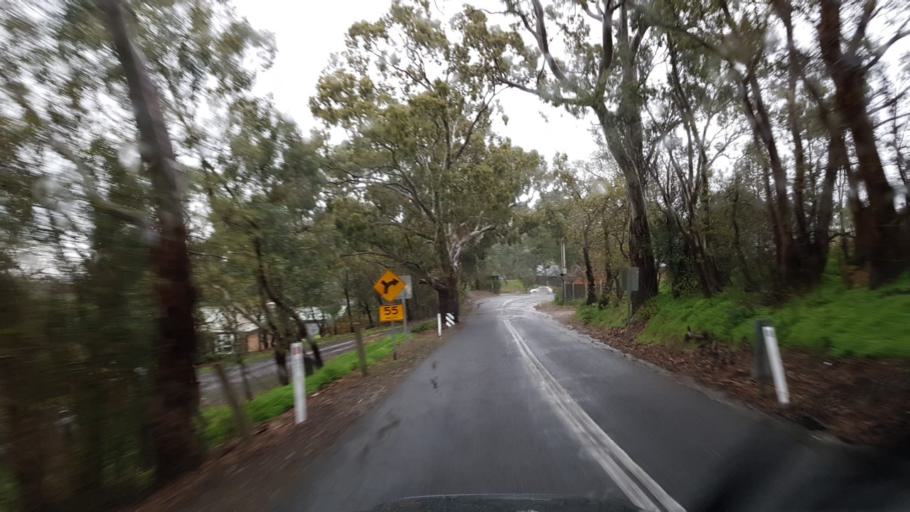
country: AU
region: South Australia
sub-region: Onkaparinga
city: Craigburn Farm
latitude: -35.0606
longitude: 138.6193
